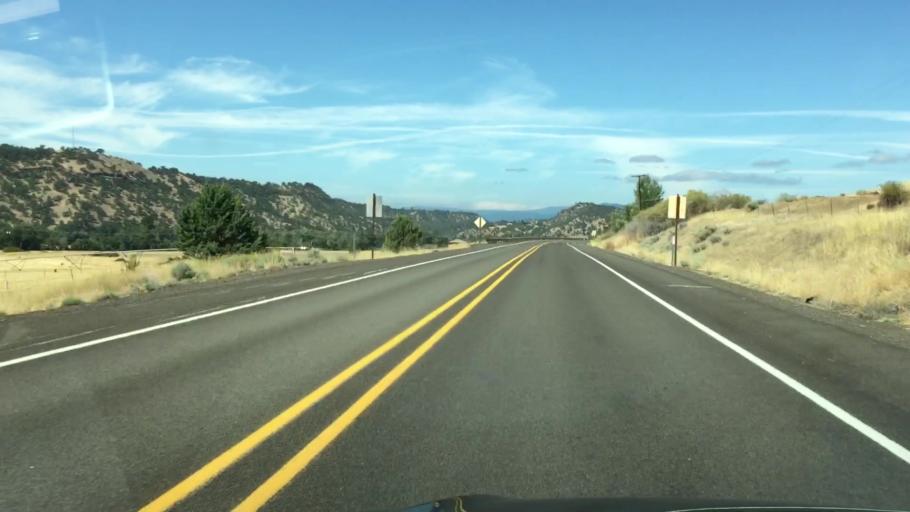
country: US
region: Oregon
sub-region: Wasco County
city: The Dalles
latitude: 45.2542
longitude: -121.1806
